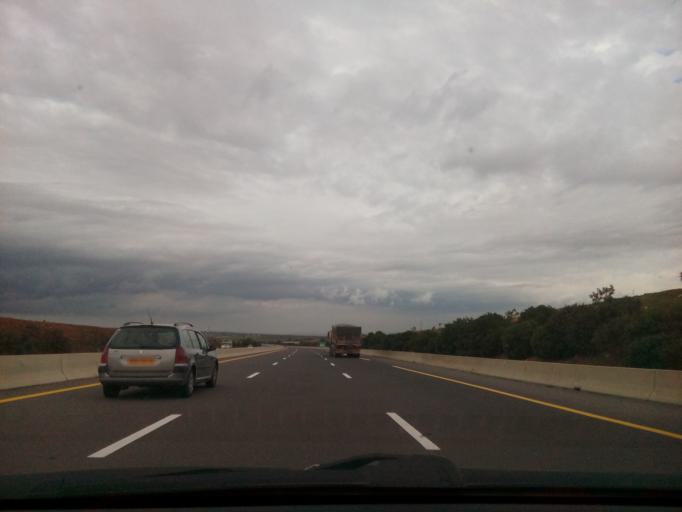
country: DZ
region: Mascara
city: Sig
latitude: 35.5142
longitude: -0.3622
